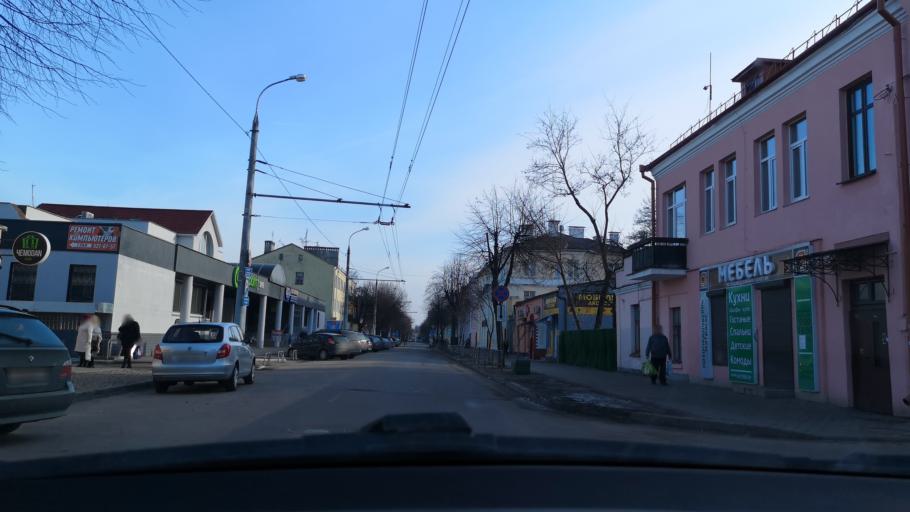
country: BY
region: Brest
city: Brest
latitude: 52.0983
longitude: 23.6849
